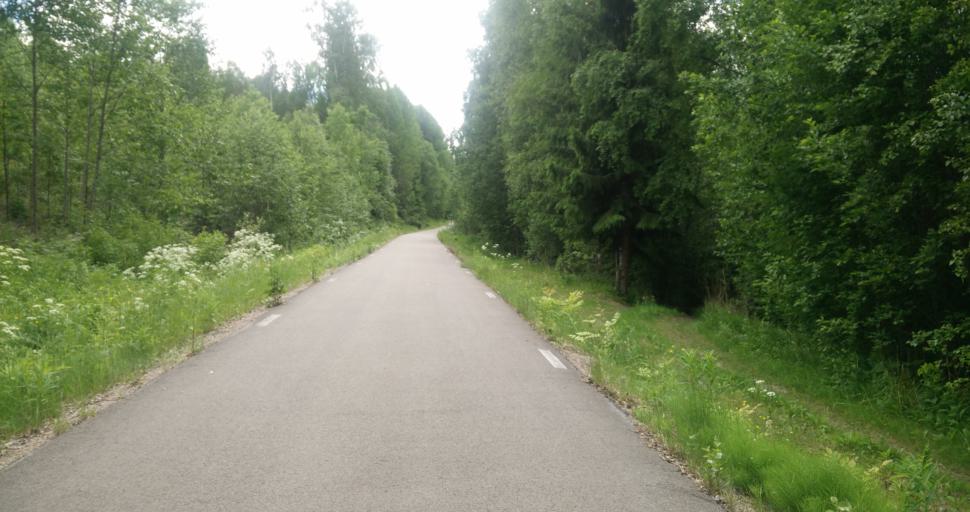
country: SE
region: Vaermland
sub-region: Hagfors Kommun
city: Hagfors
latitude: 59.9940
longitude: 13.5893
